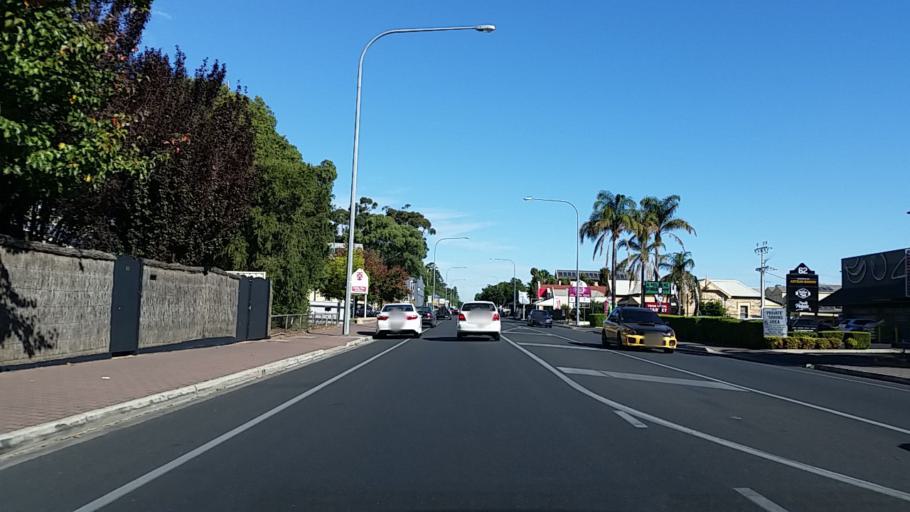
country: AU
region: South Australia
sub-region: Prospect
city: Prospect
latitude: -34.8912
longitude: 138.5943
